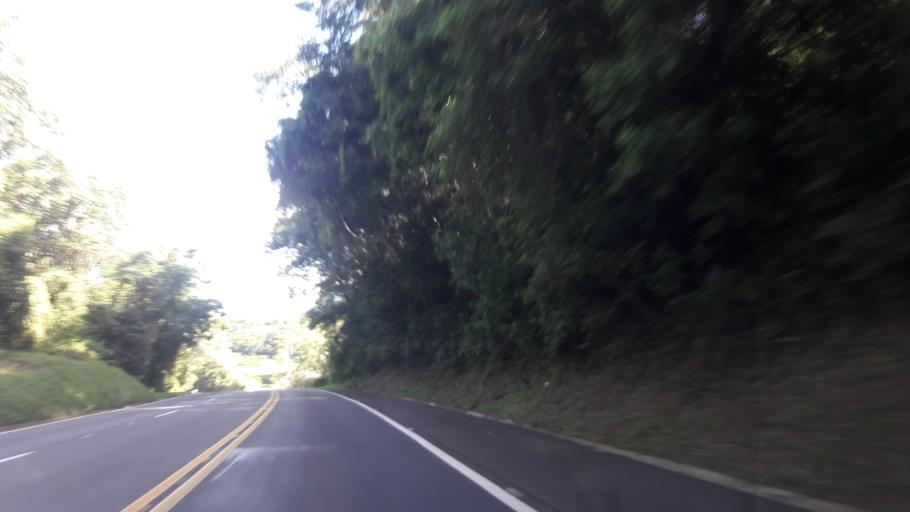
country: BR
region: Parana
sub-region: Laranjeiras Do Sul
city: Laranjeiras do Sul
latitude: -25.4095
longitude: -52.0883
